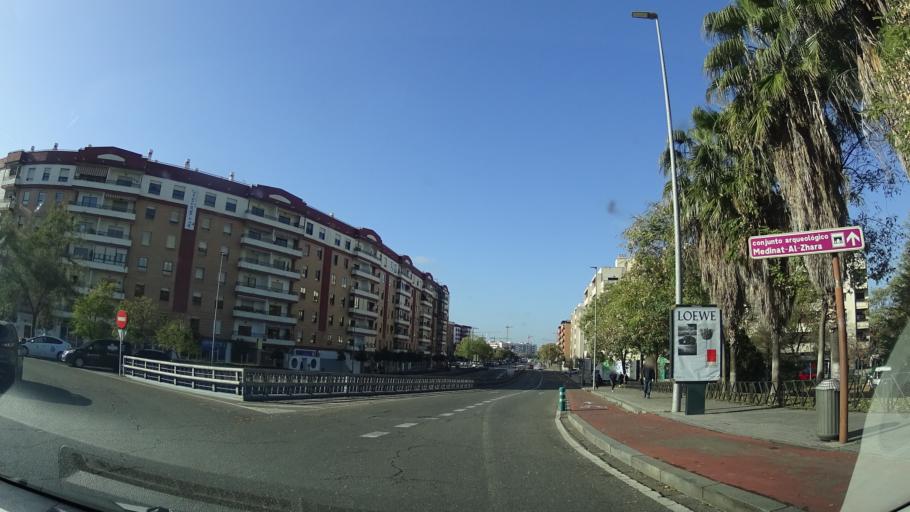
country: ES
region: Andalusia
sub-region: Province of Cordoba
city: Cordoba
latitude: 37.8852
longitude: -4.7956
